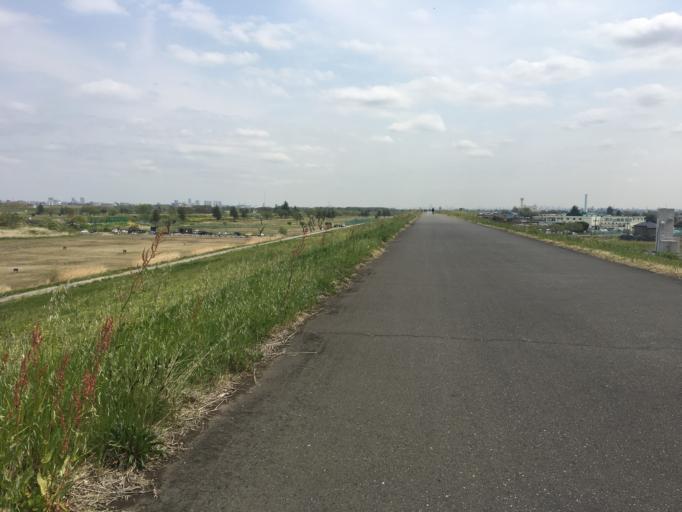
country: JP
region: Saitama
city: Shiki
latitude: 35.8794
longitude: 139.5666
